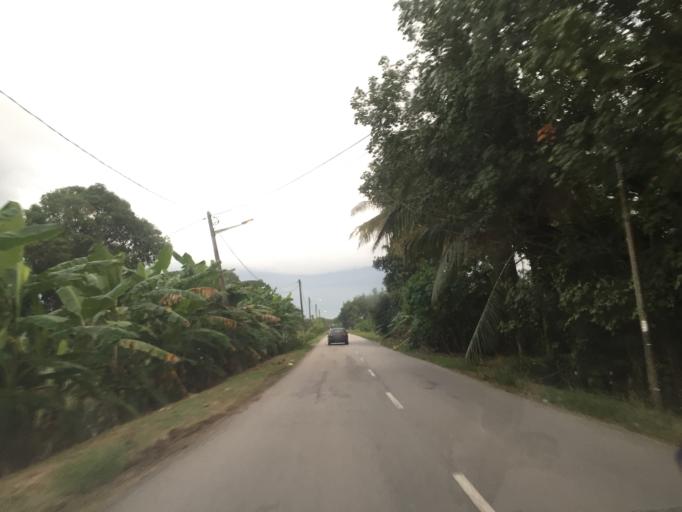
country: MY
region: Penang
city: Tasek Glugor
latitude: 5.5362
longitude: 100.5150
